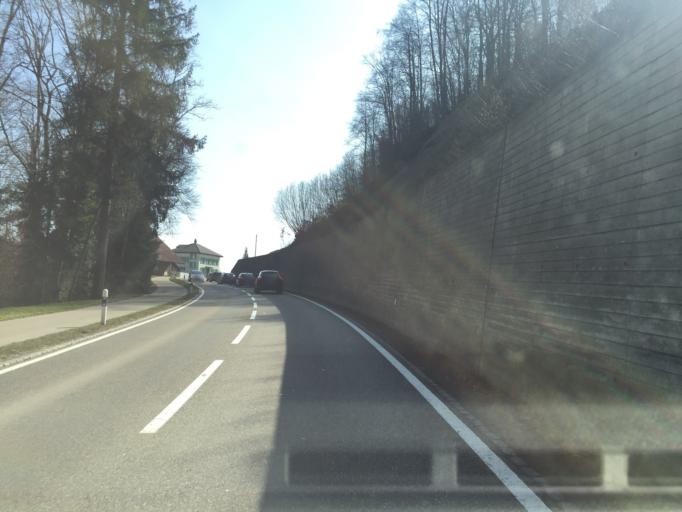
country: CH
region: Saint Gallen
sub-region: Wahlkreis Toggenburg
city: Lutisburg
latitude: 47.3917
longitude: 9.0740
